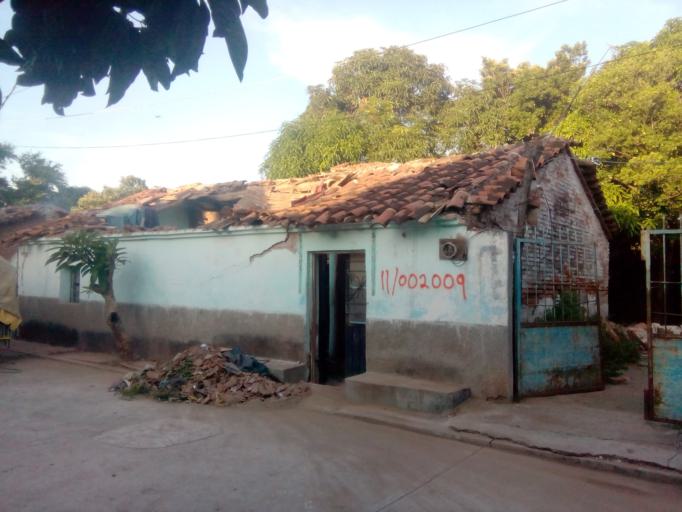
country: MX
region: Oaxaca
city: San Jeronimo Ixtepec
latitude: 16.5683
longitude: -95.1025
